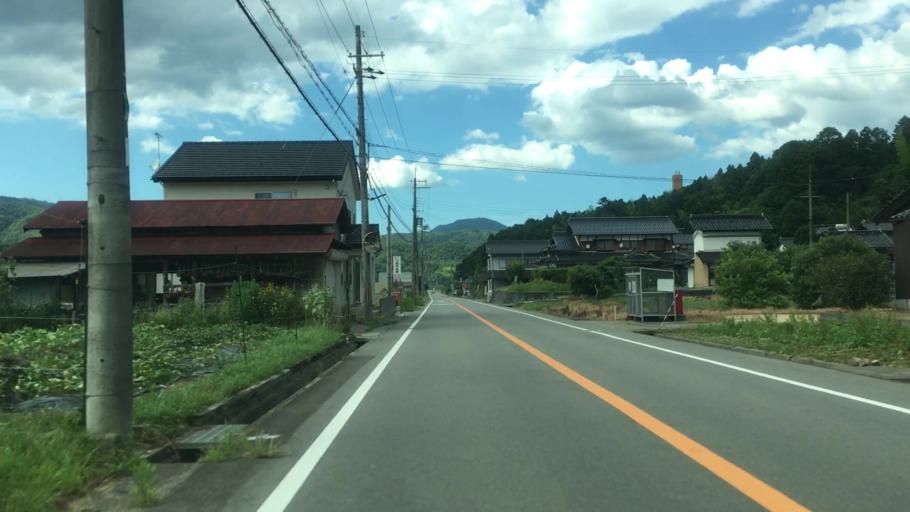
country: JP
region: Hyogo
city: Toyooka
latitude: 35.5414
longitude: 134.7902
